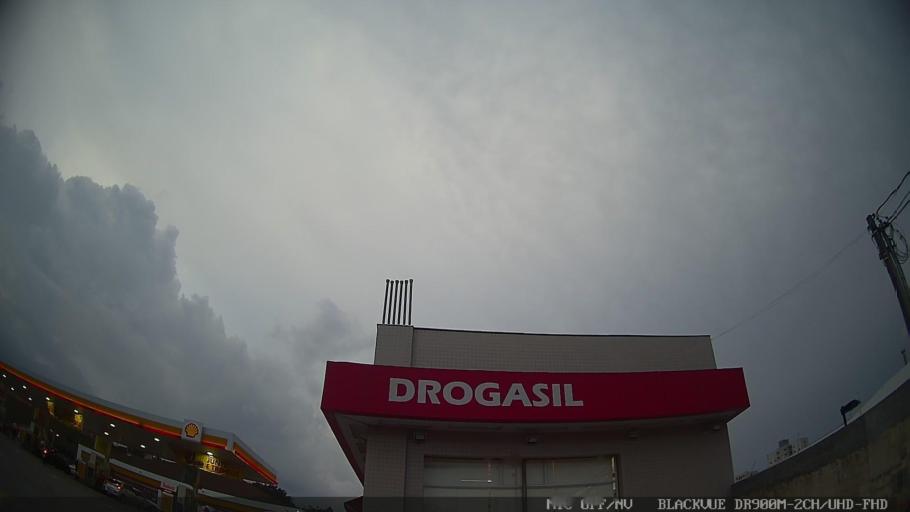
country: BR
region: Sao Paulo
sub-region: Braganca Paulista
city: Braganca Paulista
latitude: -22.9527
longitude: -46.5469
